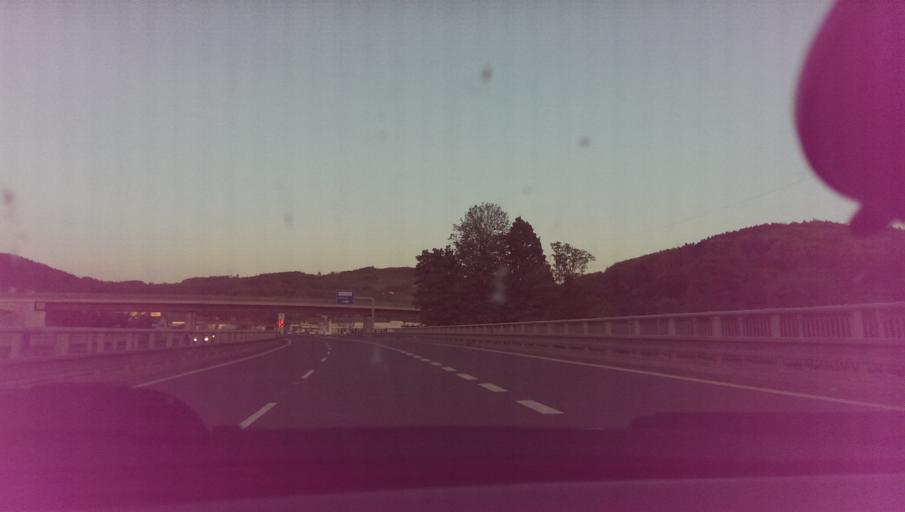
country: CZ
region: Zlin
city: Jablunka
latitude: 49.3634
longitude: 17.9513
